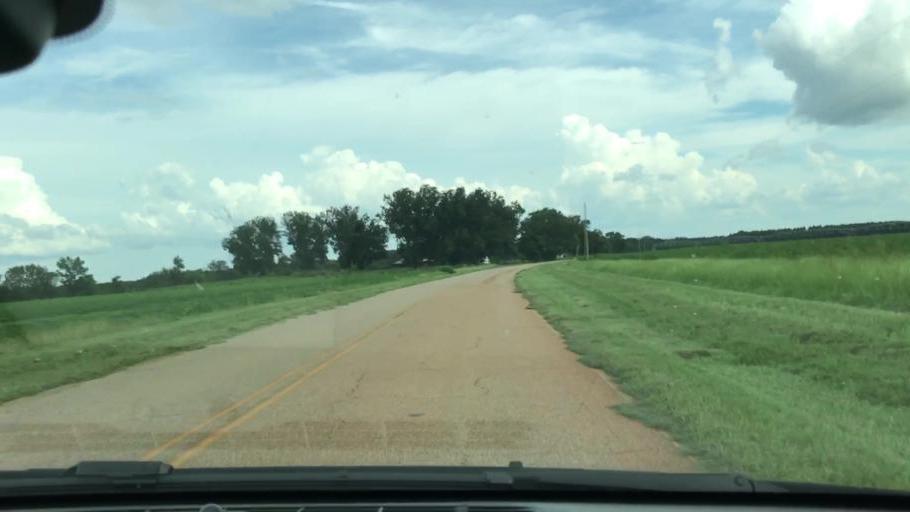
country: US
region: Georgia
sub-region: Clay County
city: Fort Gaines
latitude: 31.5679
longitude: -84.9921
